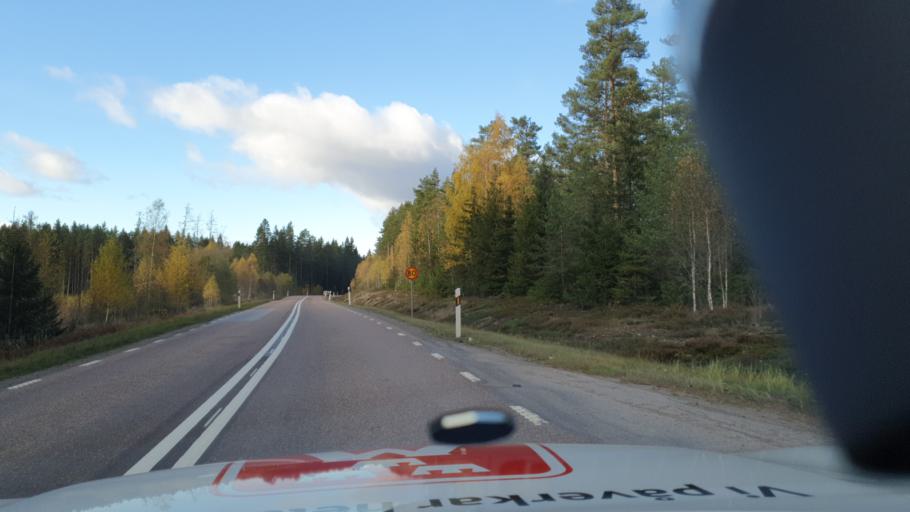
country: SE
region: Gaevleborg
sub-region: Gavle Kommun
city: Hedesunda
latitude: 60.4414
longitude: 16.9653
